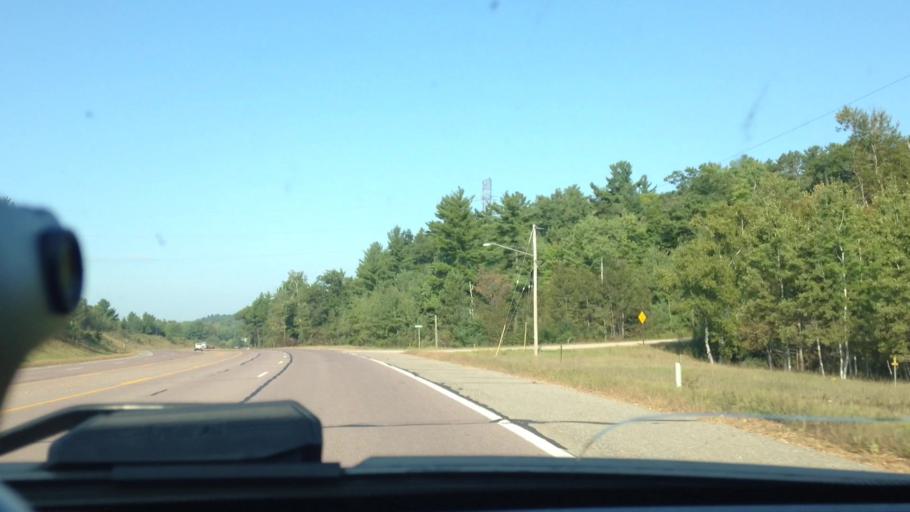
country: US
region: Michigan
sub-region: Dickinson County
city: Quinnesec
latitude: 45.8041
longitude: -87.9685
